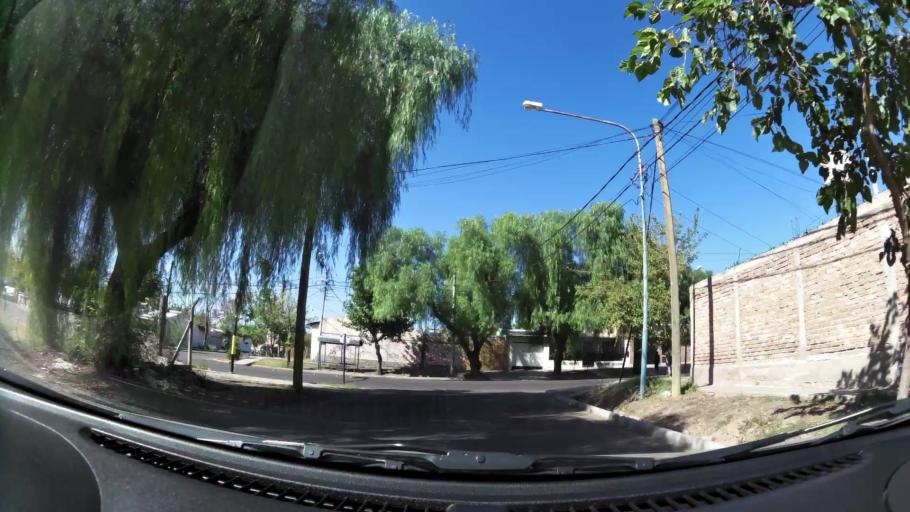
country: AR
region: Mendoza
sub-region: Departamento de Godoy Cruz
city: Godoy Cruz
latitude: -32.9013
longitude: -68.8797
